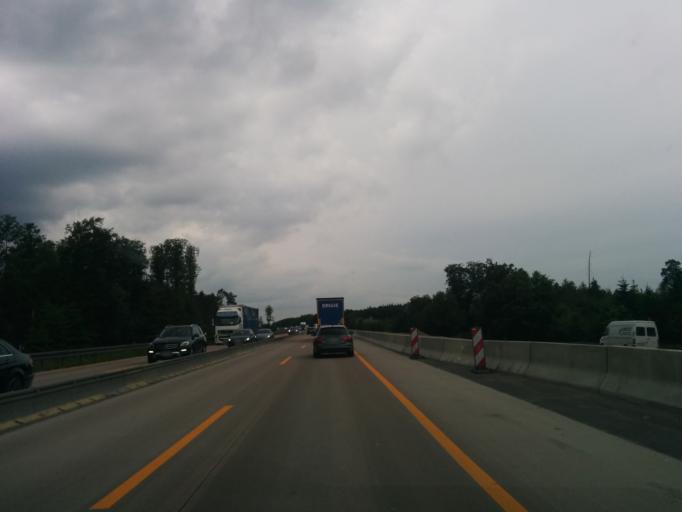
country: DE
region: Bavaria
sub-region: Swabia
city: Landensberg
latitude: 48.4065
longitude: 10.5169
